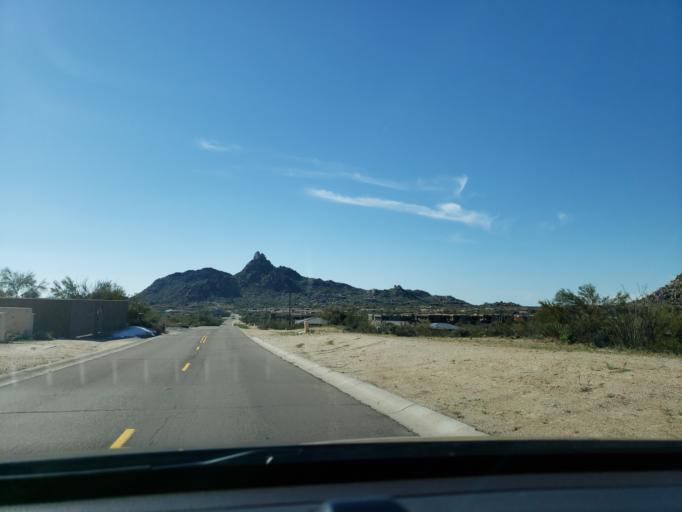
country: US
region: Arizona
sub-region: Maricopa County
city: Carefree
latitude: 33.7268
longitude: -111.8444
